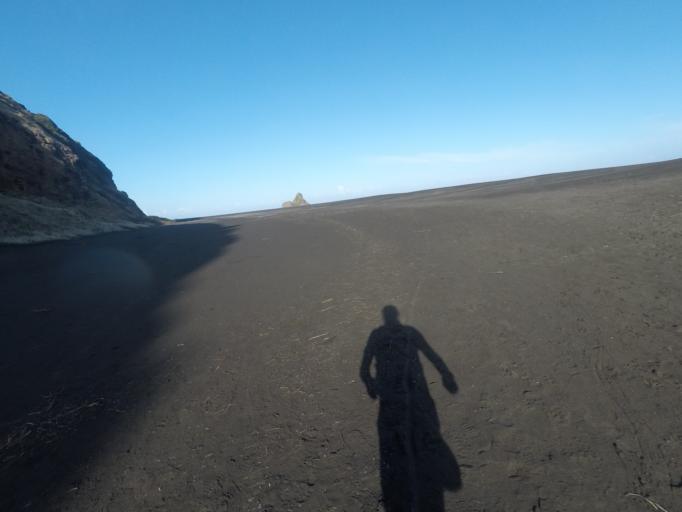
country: NZ
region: Auckland
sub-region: Auckland
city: Muriwai Beach
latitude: -36.9910
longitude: 174.4746
